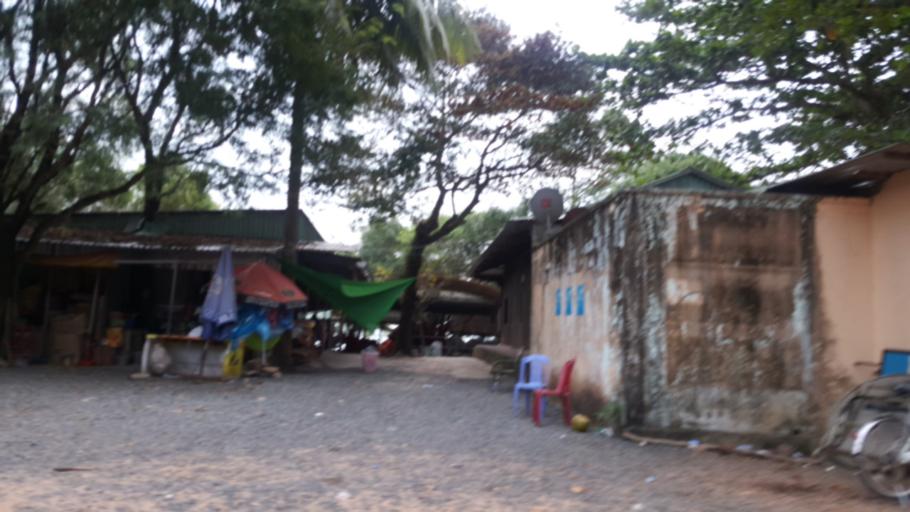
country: VN
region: Kien Giang
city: Duong GJong
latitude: 10.0563
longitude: 104.0353
